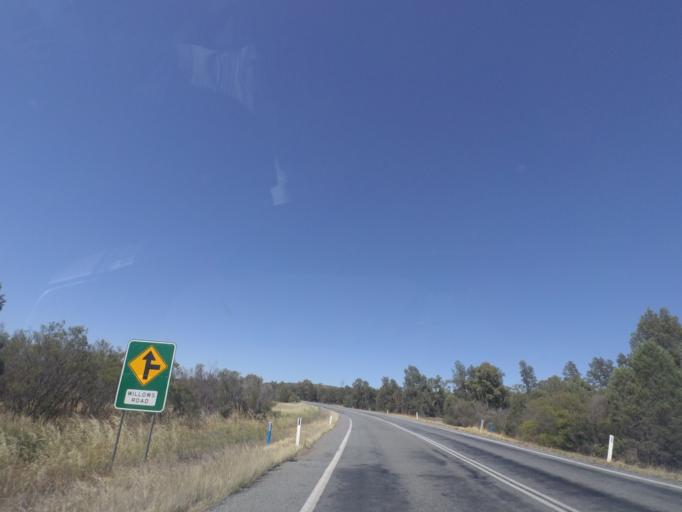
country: AU
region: New South Wales
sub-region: Narrandera
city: Narrandera
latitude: -34.4202
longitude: 146.8464
